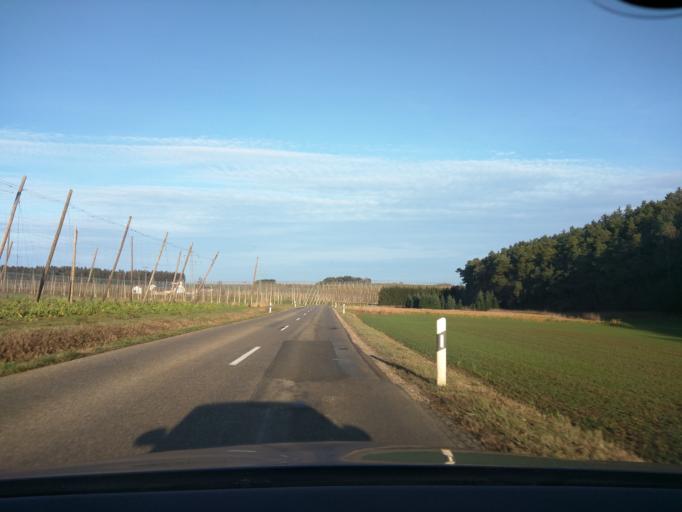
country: DE
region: Bavaria
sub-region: Upper Bavaria
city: Wolnzach
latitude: 48.5778
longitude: 11.6691
